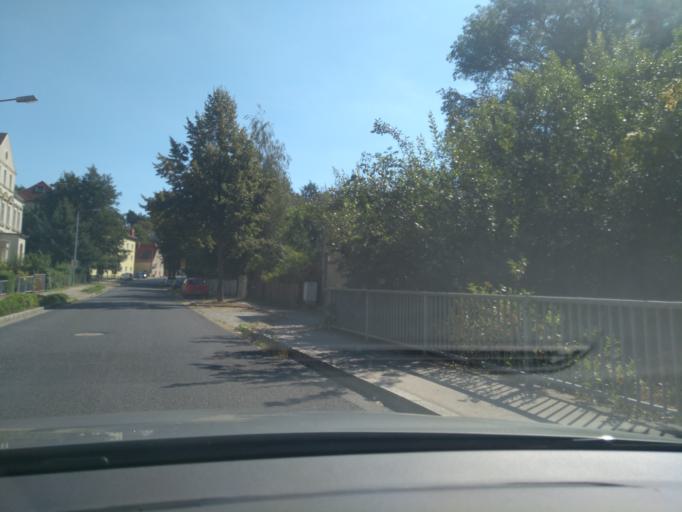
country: DE
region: Saxony
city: Kamenz
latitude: 51.2706
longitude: 14.1024
